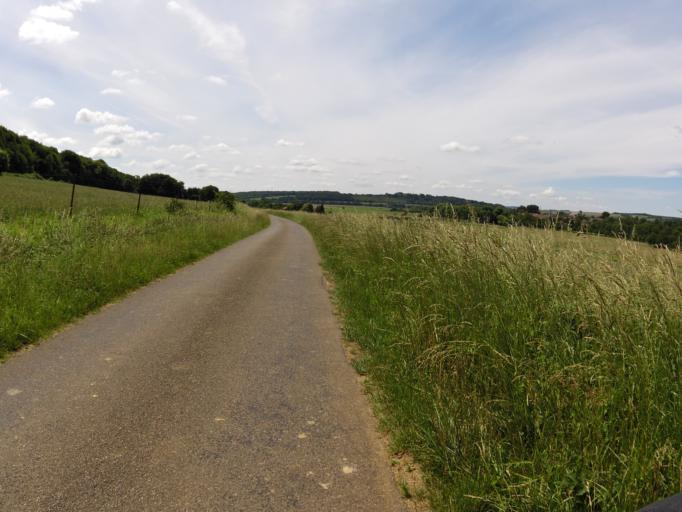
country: FR
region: Lorraine
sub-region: Departement de la Meuse
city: Stenay
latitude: 49.5384
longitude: 5.1244
